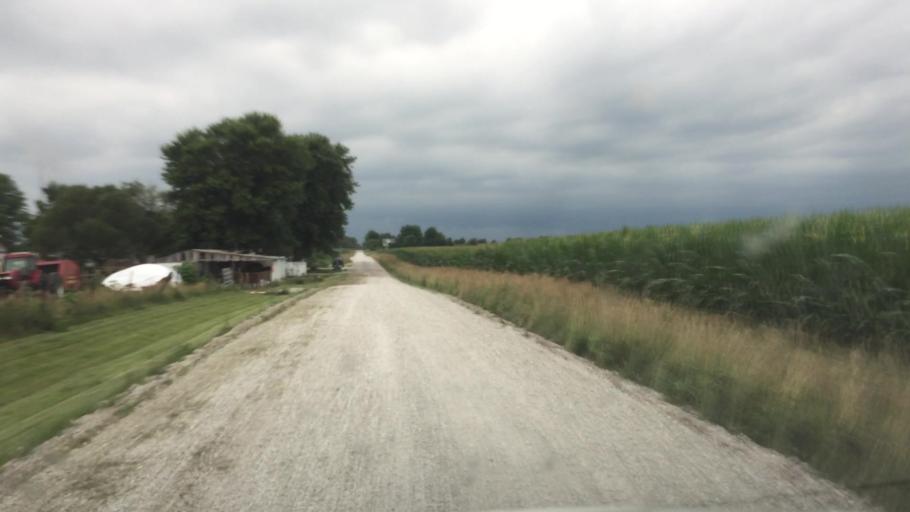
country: US
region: Illinois
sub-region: Adams County
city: Camp Point
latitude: 40.2155
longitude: -90.9626
